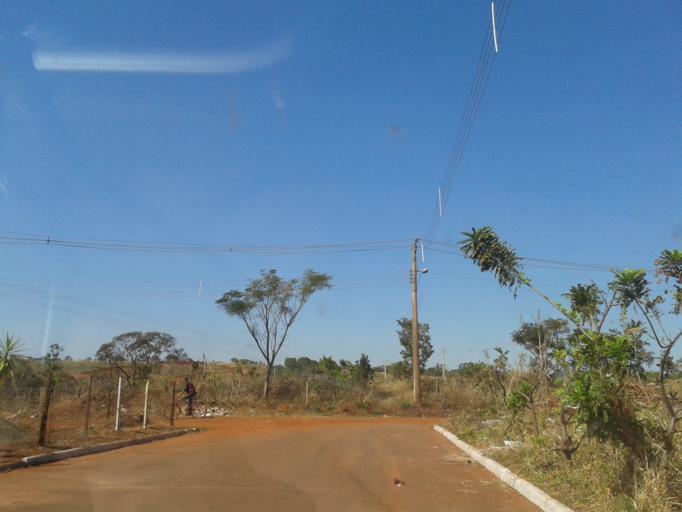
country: BR
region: Minas Gerais
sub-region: Ituiutaba
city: Ituiutaba
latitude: -18.9999
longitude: -49.4734
